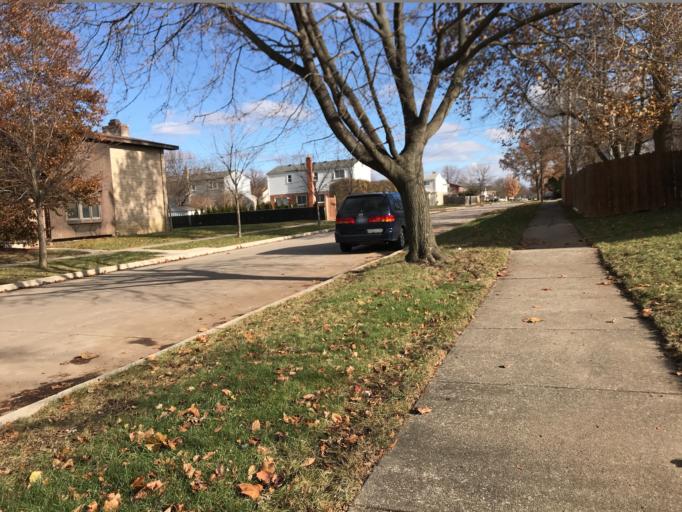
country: US
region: Michigan
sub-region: Oakland County
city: Berkley
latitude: 42.4851
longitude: -83.1991
